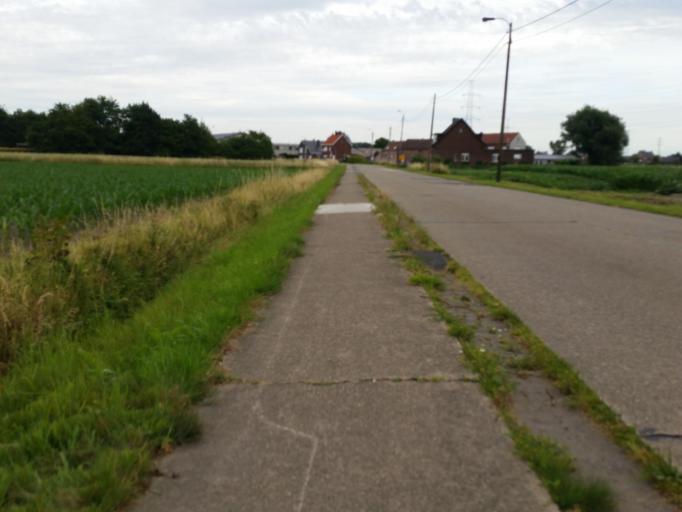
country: BE
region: Flanders
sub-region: Provincie Vlaams-Brabant
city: Kapelle-op-den-Bos
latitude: 51.0296
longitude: 4.3800
